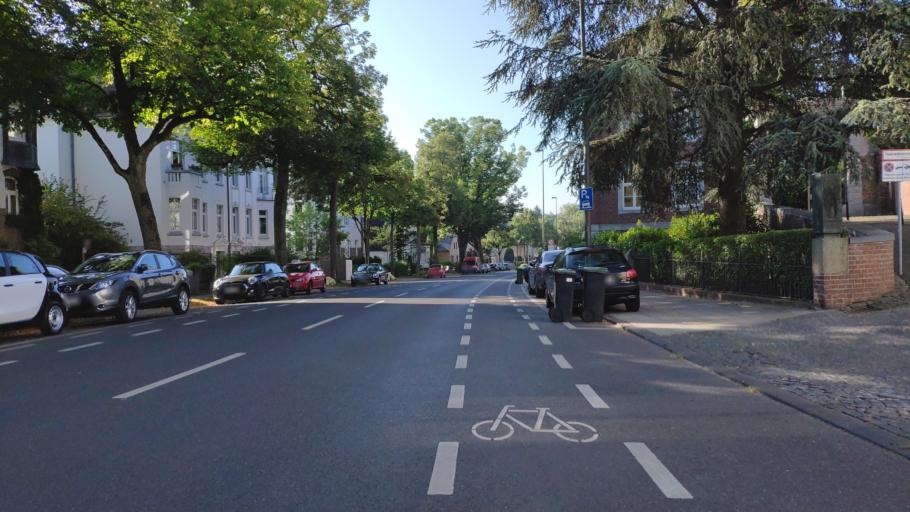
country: DE
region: North Rhine-Westphalia
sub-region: Regierungsbezirk Koln
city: Aachen
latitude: 50.7555
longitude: 6.0855
